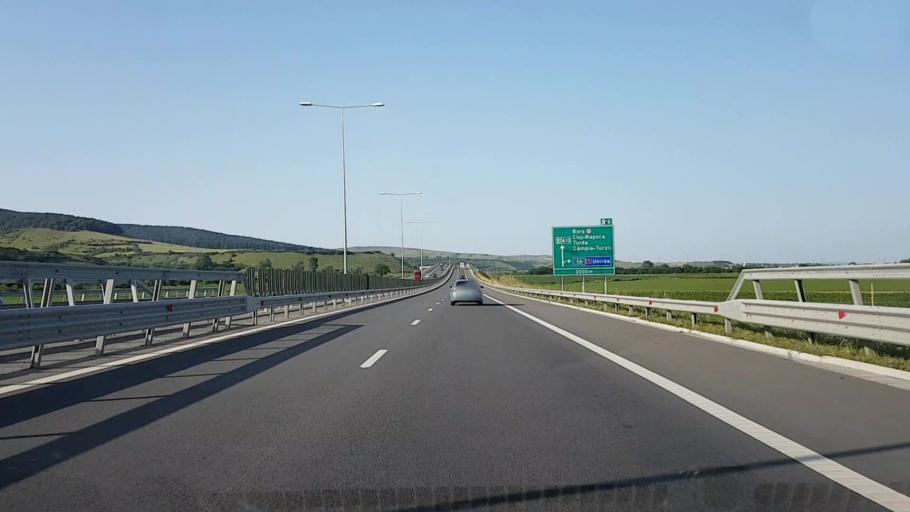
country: RO
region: Alba
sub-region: Comuna Miraslau
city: Miraslau
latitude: 46.3662
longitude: 23.7366
